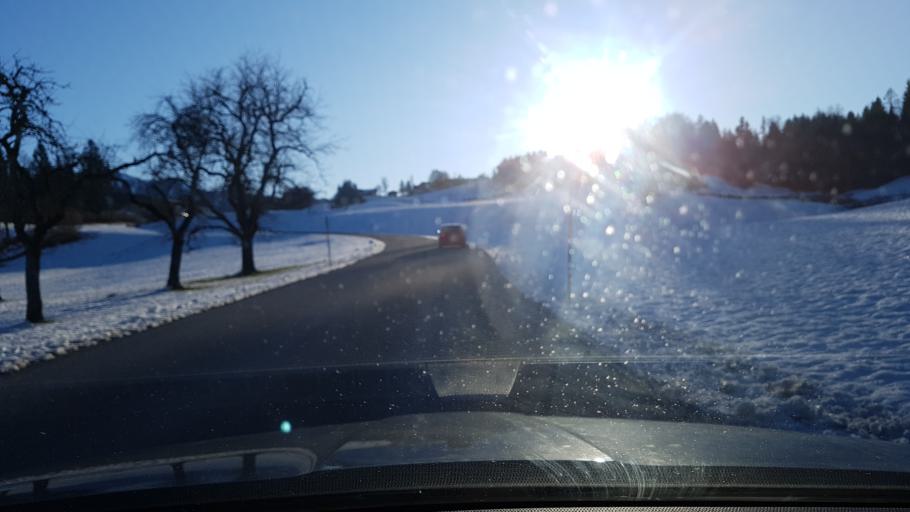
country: AT
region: Salzburg
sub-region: Politischer Bezirk Hallein
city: Kuchl
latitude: 47.6590
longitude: 13.1850
